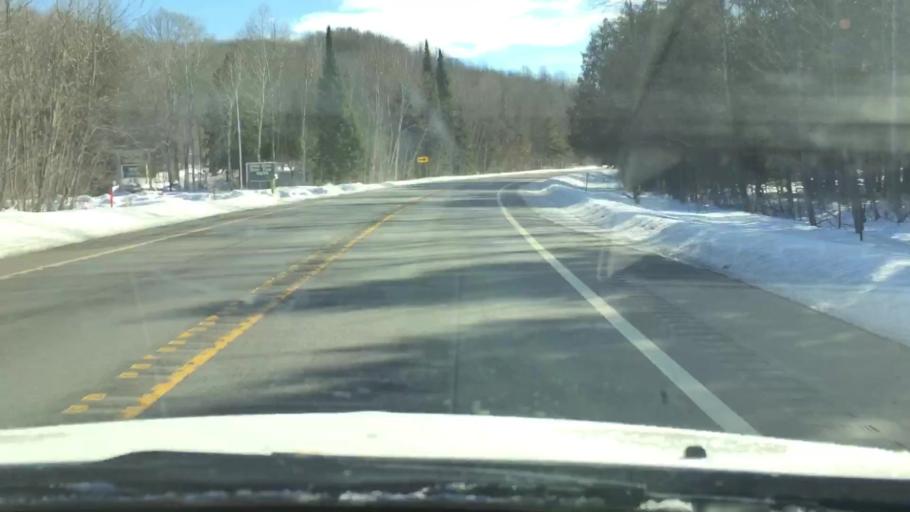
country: US
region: Michigan
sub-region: Antrim County
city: Mancelona
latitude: 45.0062
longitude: -85.0634
